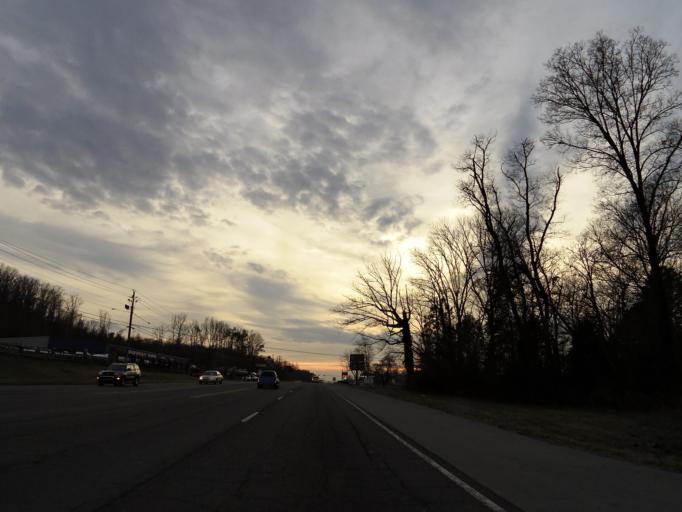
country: US
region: Tennessee
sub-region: Monroe County
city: Madisonville
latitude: 35.5420
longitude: -84.3263
